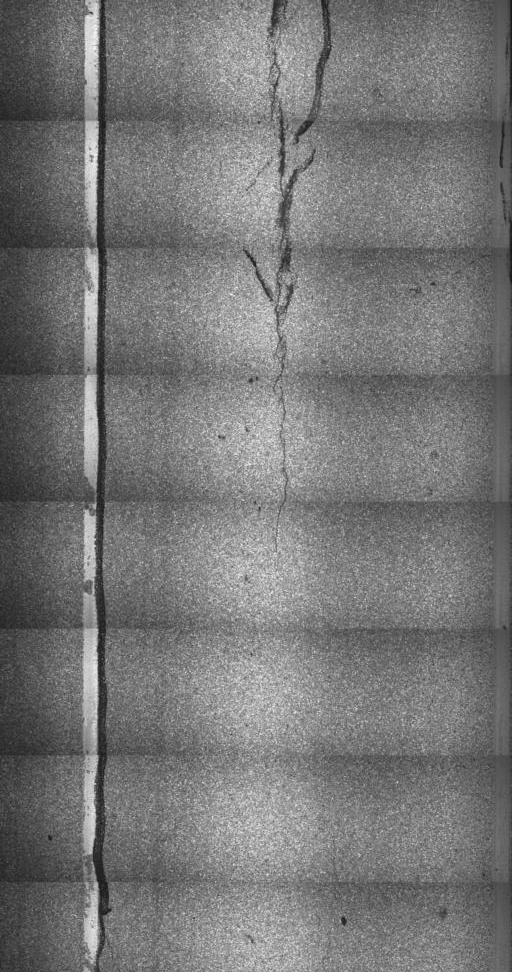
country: US
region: Vermont
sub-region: Franklin County
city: Swanton
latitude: 44.8703
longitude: -73.0981
